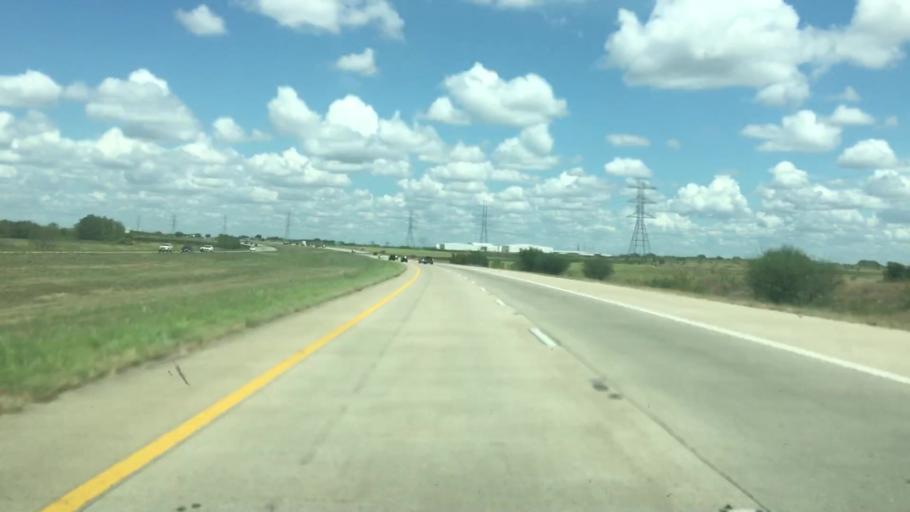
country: US
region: Texas
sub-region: Travis County
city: Manor
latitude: 30.3836
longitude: -97.5793
